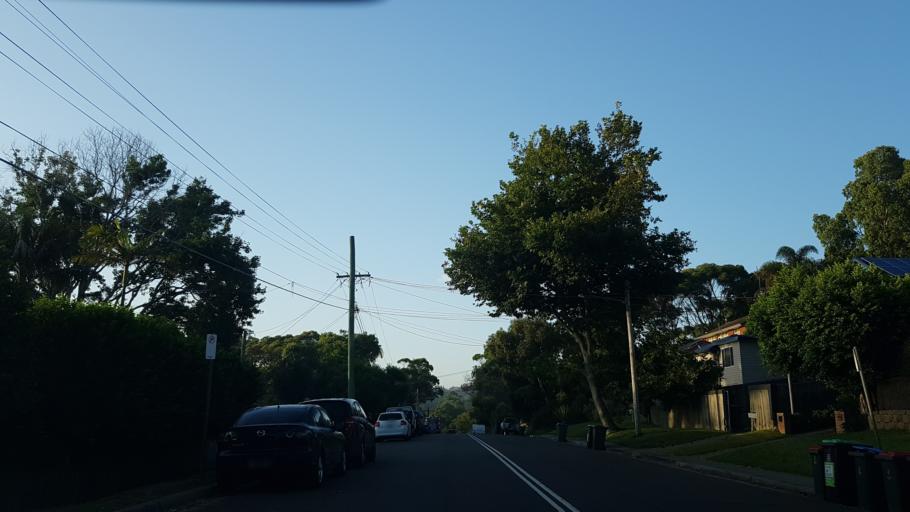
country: AU
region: New South Wales
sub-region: Warringah
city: Narraweena
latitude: -33.7331
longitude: 151.2730
